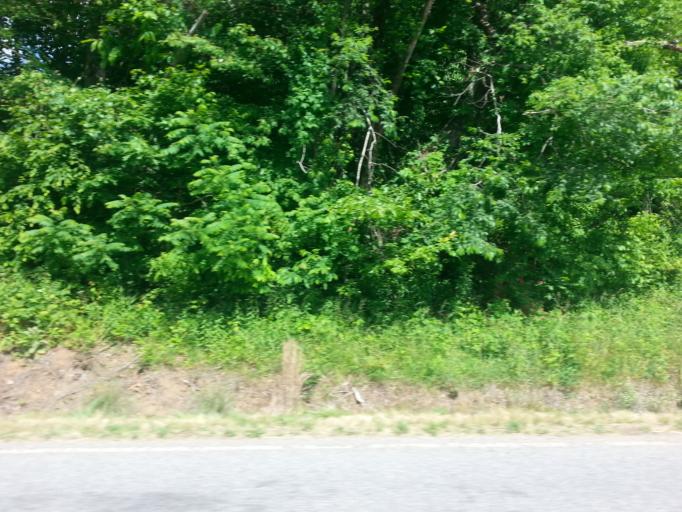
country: US
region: Georgia
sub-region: Towns County
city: Hiawassee
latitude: 34.8771
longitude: -83.7187
